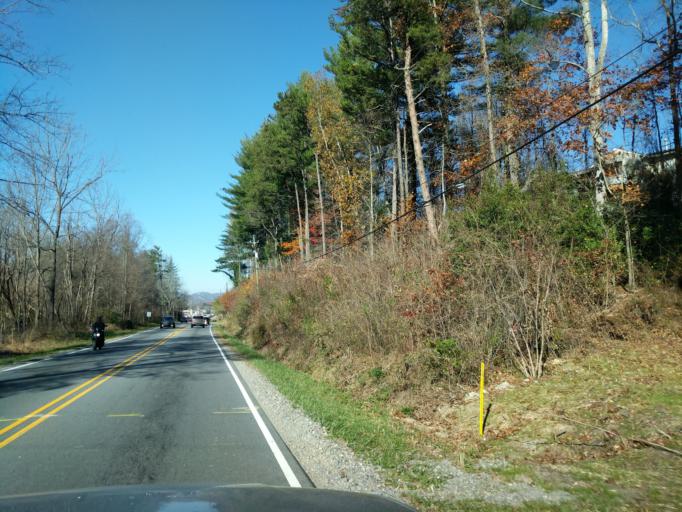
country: US
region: North Carolina
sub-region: Buncombe County
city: Biltmore Forest
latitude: 35.5298
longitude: -82.5179
